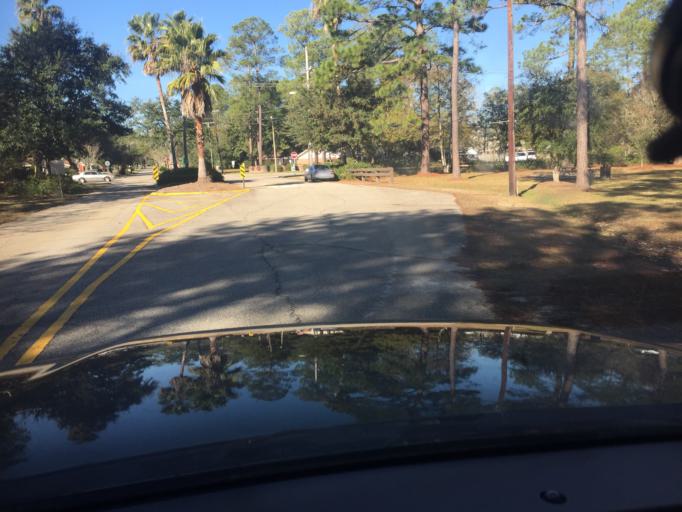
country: US
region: Louisiana
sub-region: Saint Tammany Parish
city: Slidell
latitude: 30.3054
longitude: -89.7492
